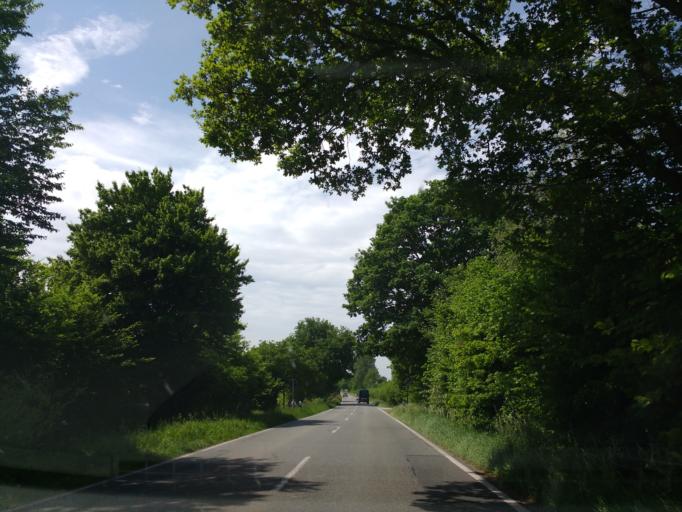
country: DE
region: Schleswig-Holstein
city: Braak
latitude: 53.6149
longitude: 10.2770
